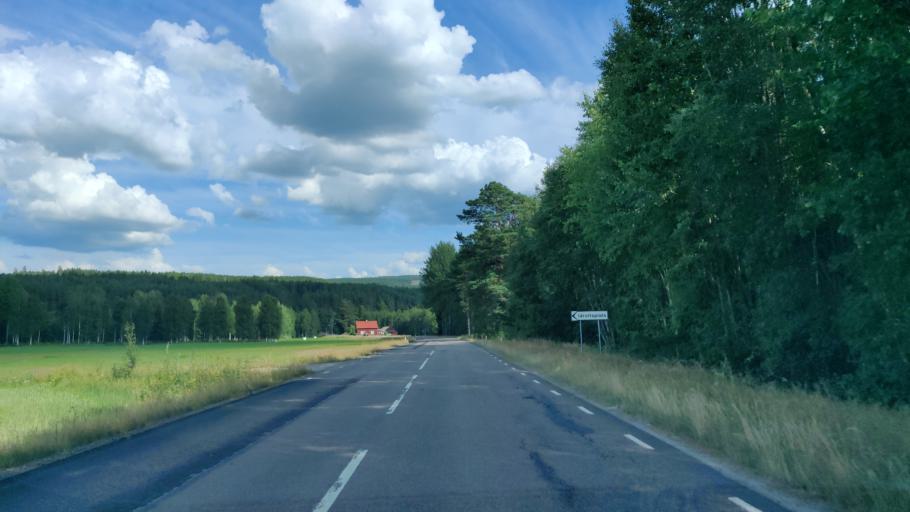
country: SE
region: Vaermland
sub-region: Hagfors Kommun
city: Ekshaerad
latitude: 60.1778
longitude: 13.5180
